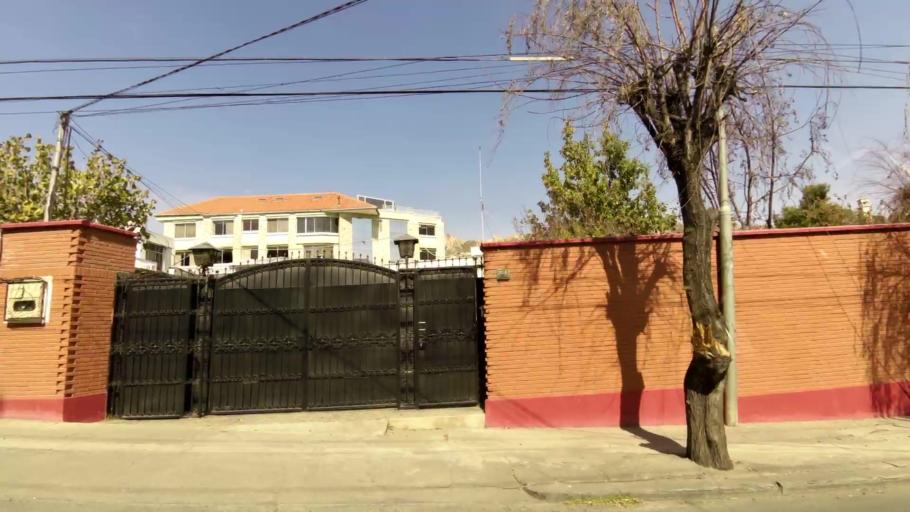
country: BO
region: La Paz
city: La Paz
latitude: -16.5445
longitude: -68.0885
